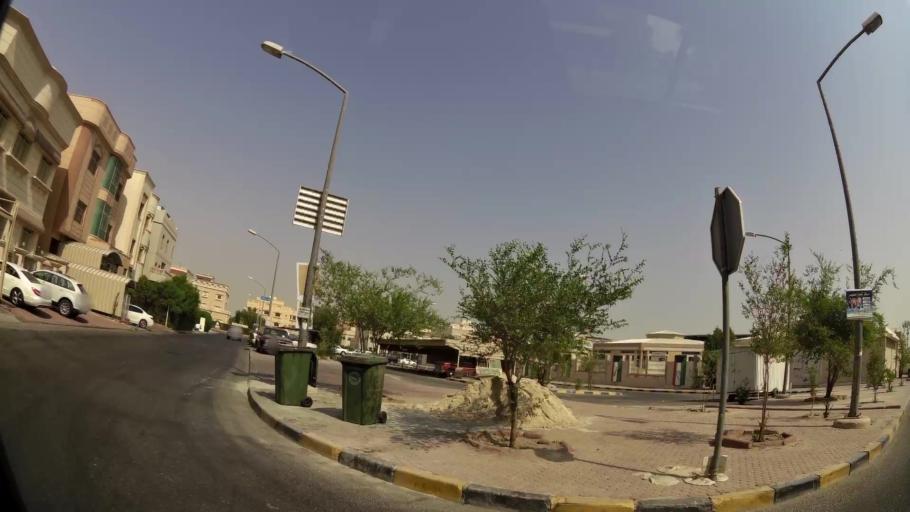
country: KW
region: Muhafazat al Jahra'
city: Al Jahra'
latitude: 29.3051
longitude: 47.7212
